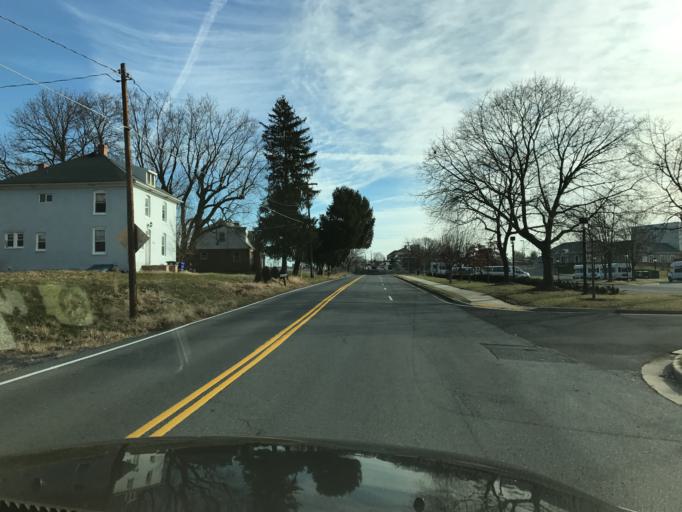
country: US
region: Maryland
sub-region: Frederick County
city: Clover Hill
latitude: 39.4363
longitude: -77.4396
